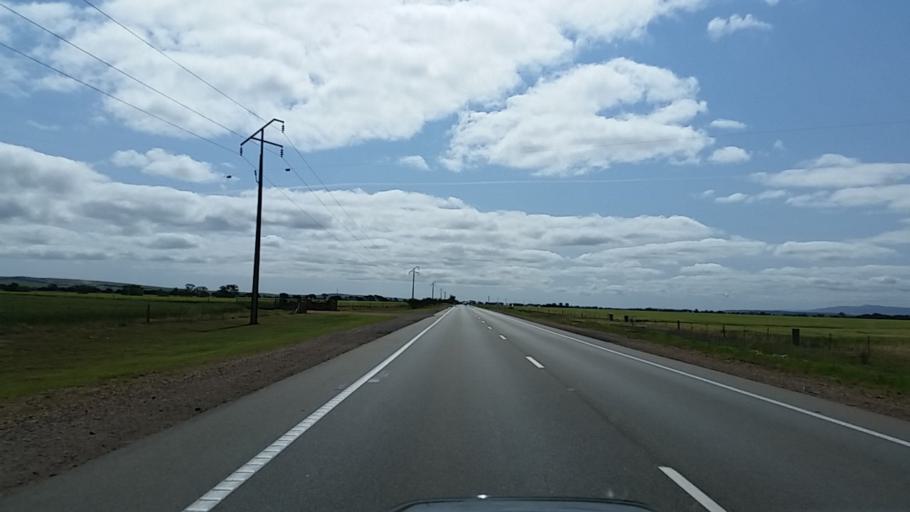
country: AU
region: South Australia
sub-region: Port Pirie City and Dists
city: Crystal Brook
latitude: -33.4785
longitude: 138.1701
